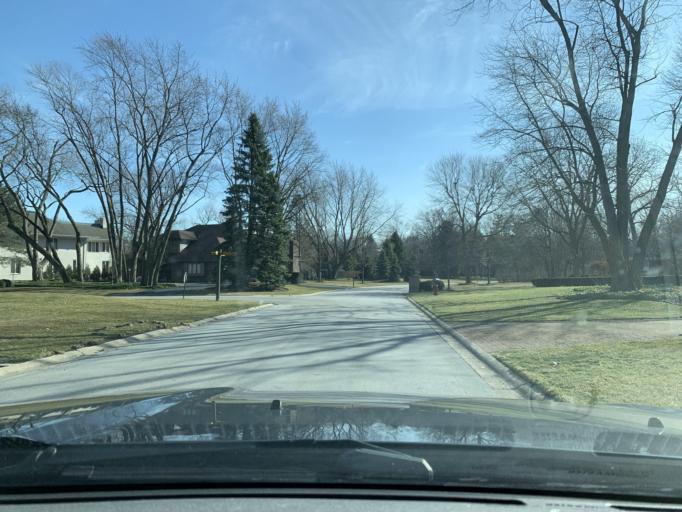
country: US
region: Indiana
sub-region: Lake County
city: Dyer
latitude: 41.5162
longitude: -87.4839
